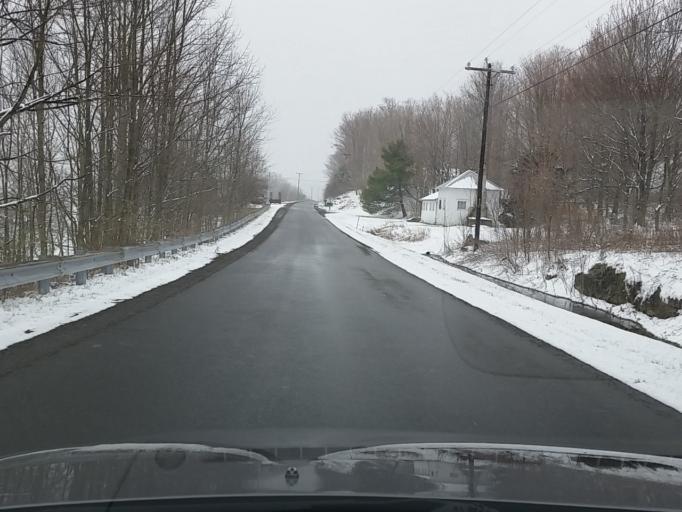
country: US
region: Pennsylvania
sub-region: Sullivan County
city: Laporte
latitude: 41.3831
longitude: -76.5126
